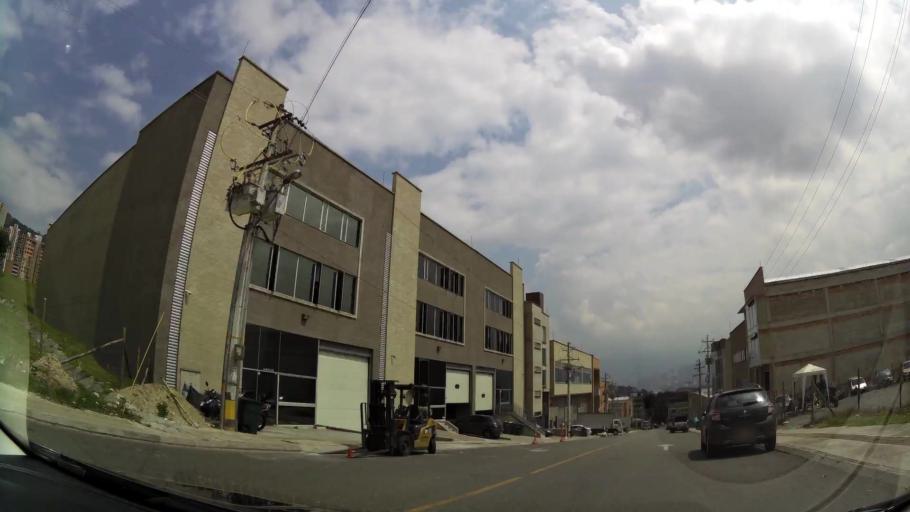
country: CO
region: Antioquia
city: Itagui
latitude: 6.1874
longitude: -75.6013
